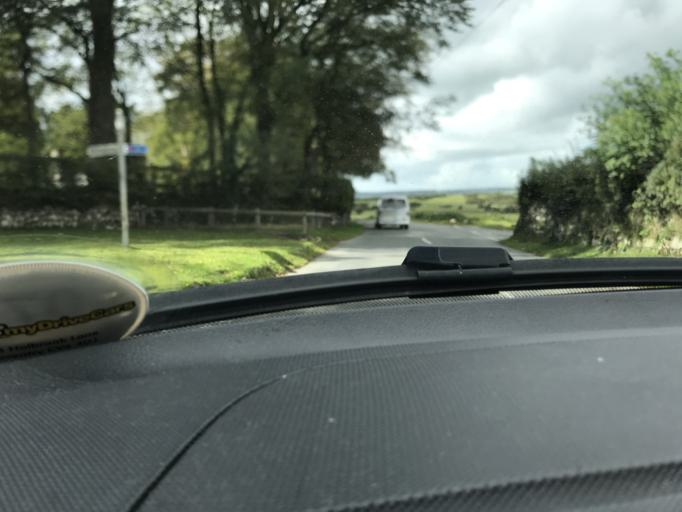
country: GB
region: England
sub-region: Devon
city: Horrabridge
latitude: 50.5409
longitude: -4.0985
